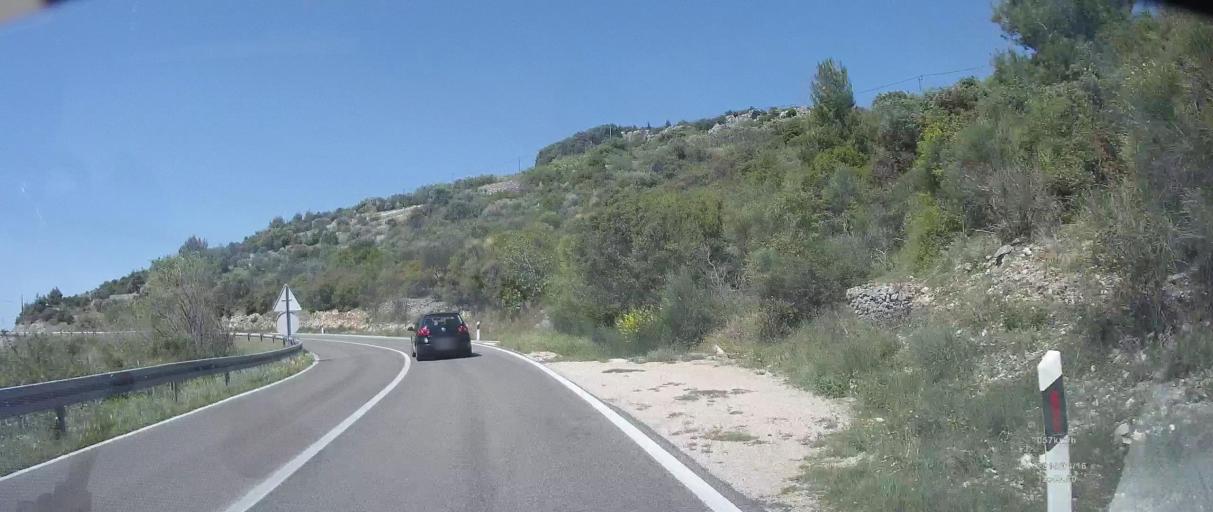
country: HR
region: Sibensko-Kniniska
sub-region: Grad Sibenik
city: Brodarica
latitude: 43.6737
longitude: 16.0222
